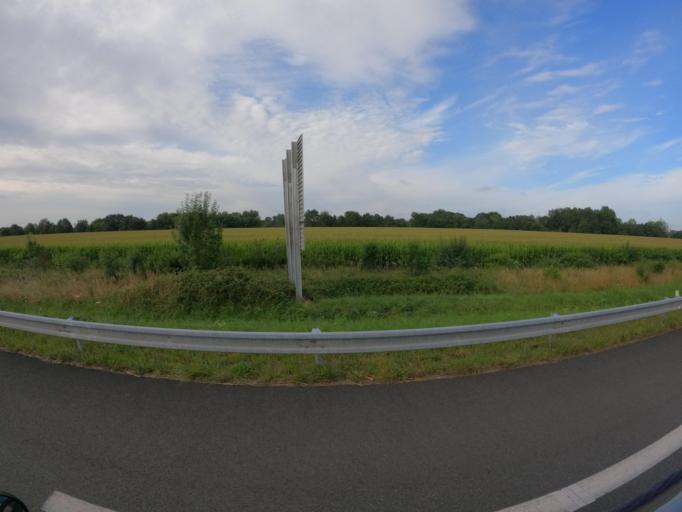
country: FR
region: Centre
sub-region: Departement d'Indre-et-Loire
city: Saint-Nicolas-de-Bourgueil
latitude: 47.2748
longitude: 0.1023
